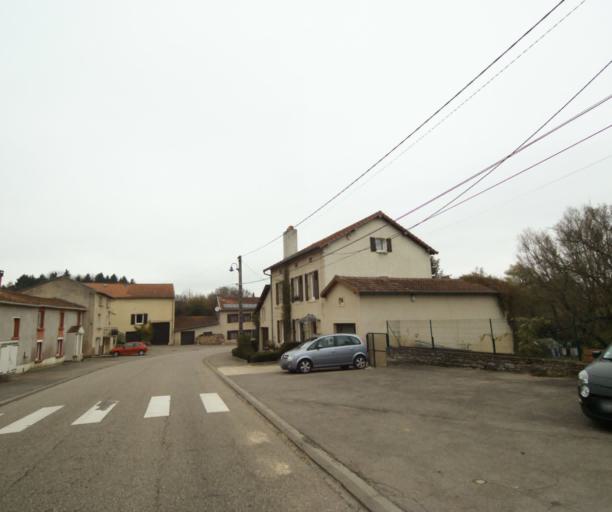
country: FR
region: Lorraine
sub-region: Departement de Meurthe-et-Moselle
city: Briey
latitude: 49.2664
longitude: 5.9142
